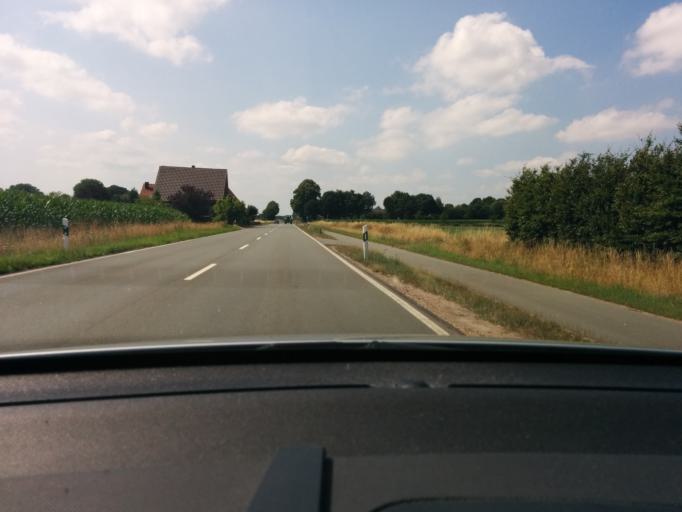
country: DE
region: North Rhine-Westphalia
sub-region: Regierungsbezirk Munster
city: Steinfurt
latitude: 52.1603
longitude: 7.3145
